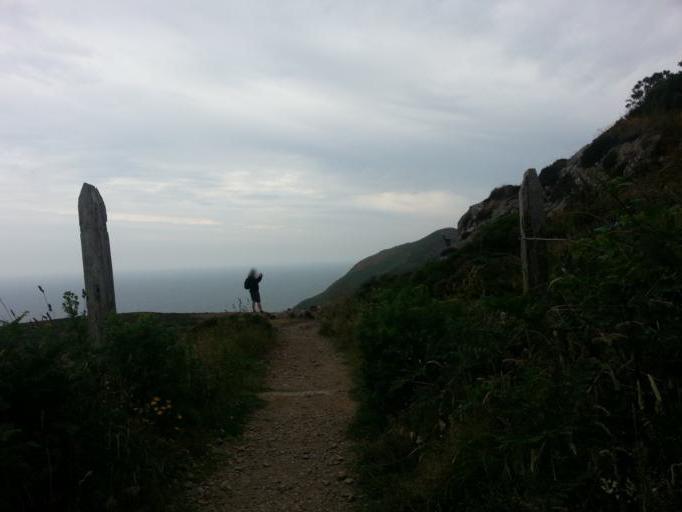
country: IE
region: Leinster
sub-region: Wicklow
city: Bray
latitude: 53.1892
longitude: -6.0832
